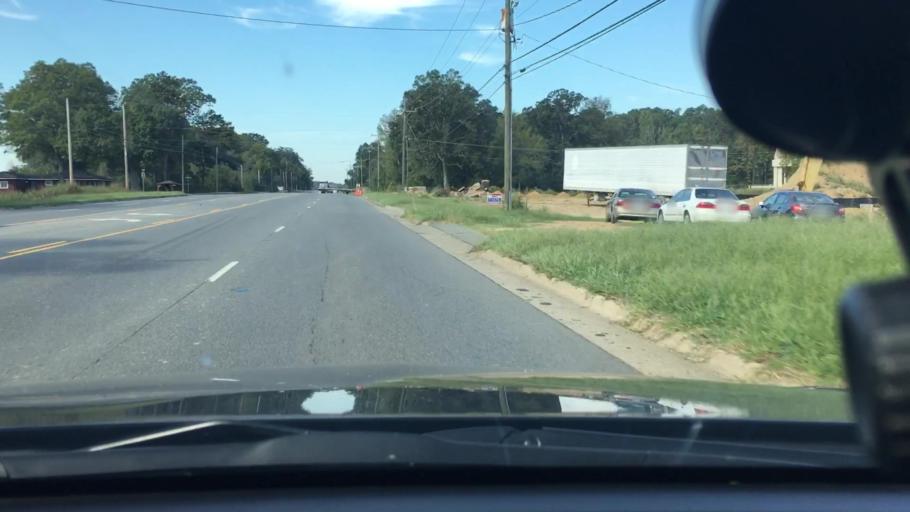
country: US
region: North Carolina
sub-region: Cabarrus County
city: Midland
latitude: 35.2538
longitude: -80.4889
